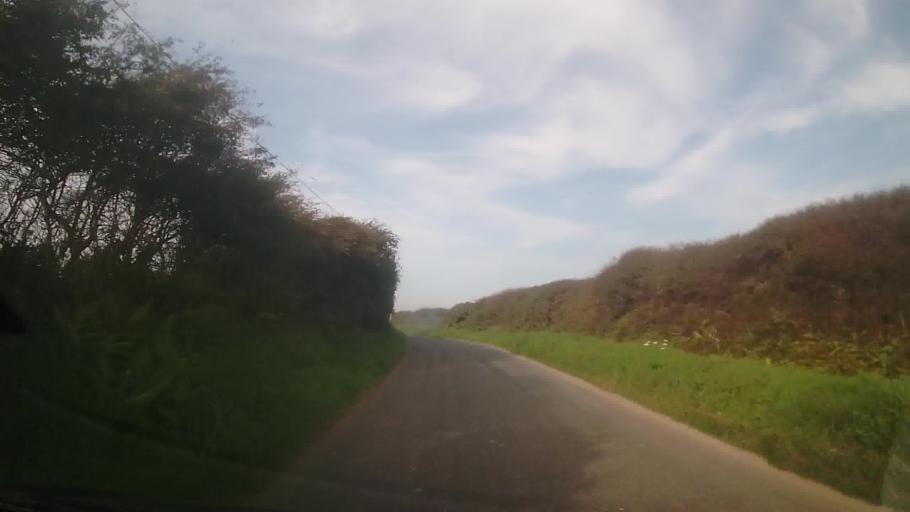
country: GB
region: Wales
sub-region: Pembrokeshire
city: Camrose
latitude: 51.8665
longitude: -5.0512
